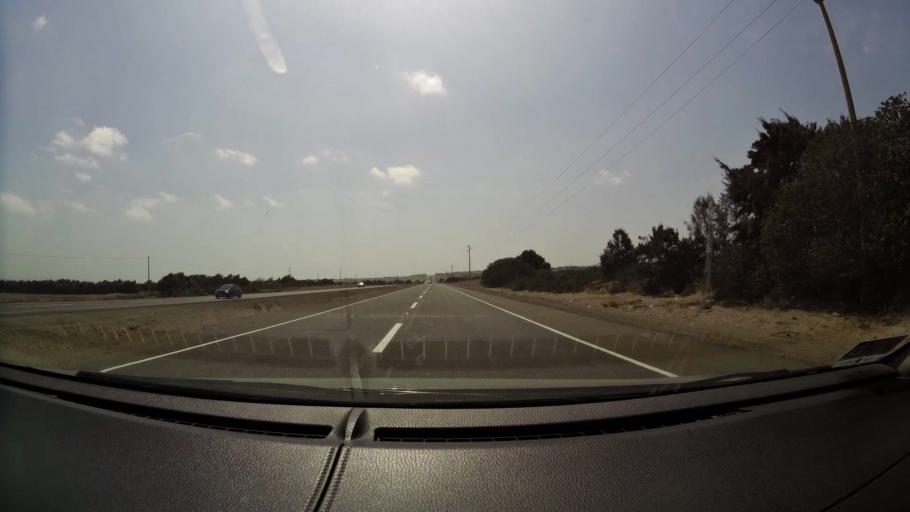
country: PE
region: Lima
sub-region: Huaura
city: Huacho
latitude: -11.2116
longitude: -77.5567
